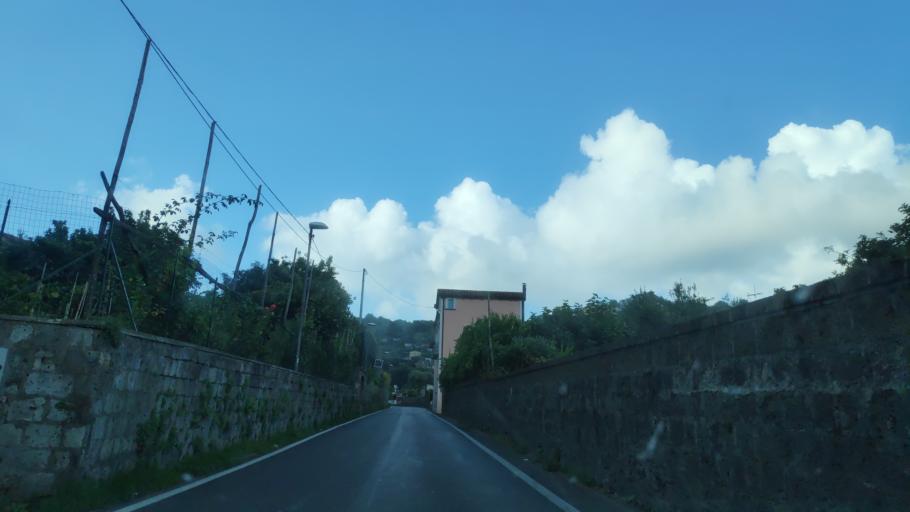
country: IT
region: Campania
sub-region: Provincia di Napoli
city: Piano di Sorrento
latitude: 40.6254
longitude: 14.4237
